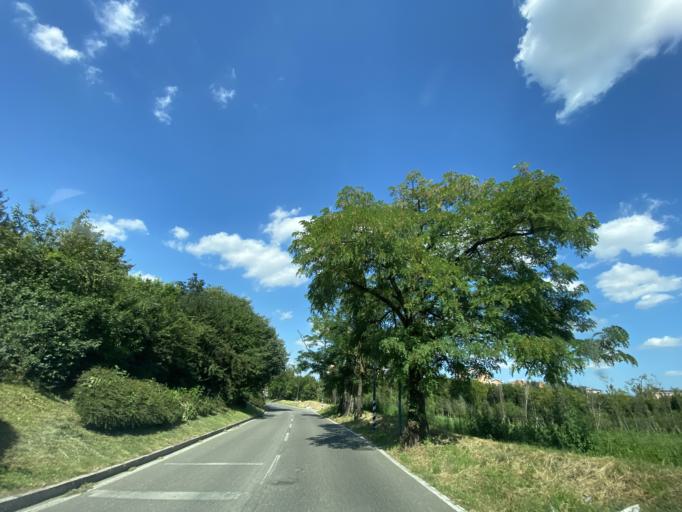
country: IT
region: Lombardy
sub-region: Citta metropolitana di Milano
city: Bresso
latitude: 45.5165
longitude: 9.1835
